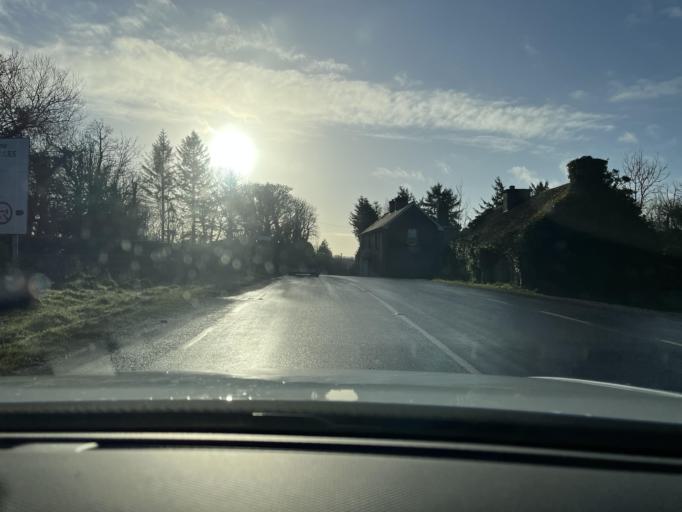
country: IE
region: Connaught
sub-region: County Leitrim
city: Manorhamilton
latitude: 54.2222
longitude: -8.2083
